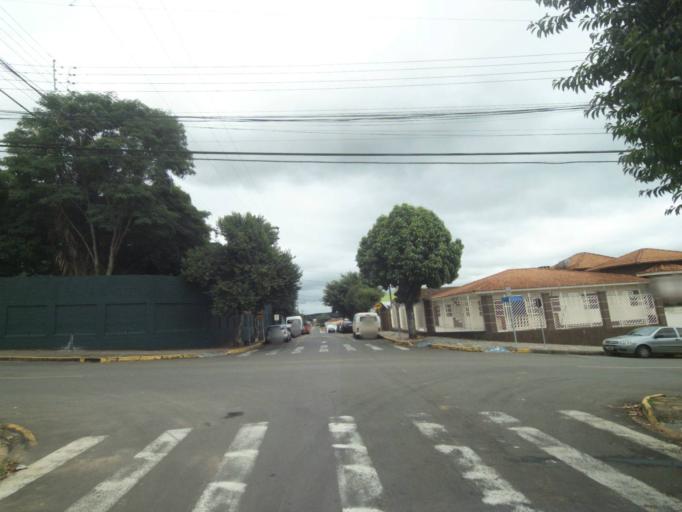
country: BR
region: Parana
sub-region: Telemaco Borba
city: Telemaco Borba
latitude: -24.3262
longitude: -50.6160
